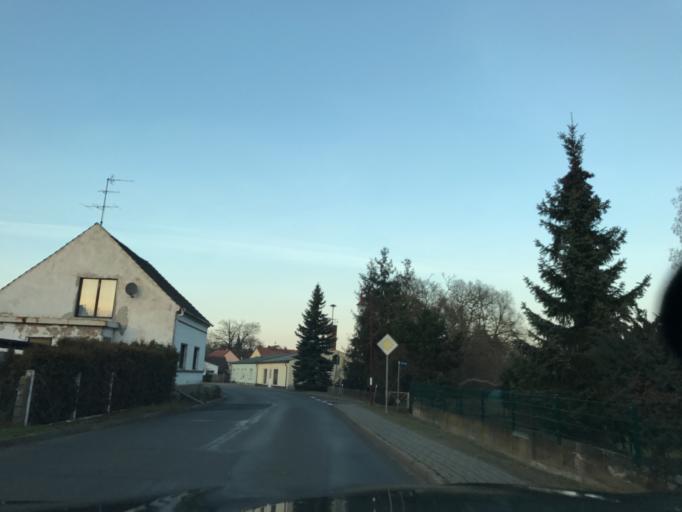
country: DE
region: Brandenburg
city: Wusterwitz
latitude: 52.4397
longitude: 12.4266
